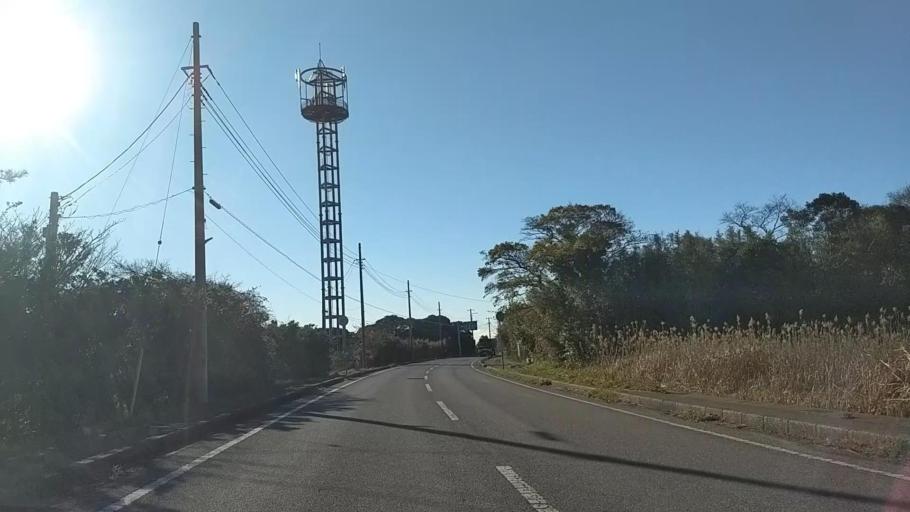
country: JP
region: Chiba
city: Futtsu
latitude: 35.3117
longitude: 139.8274
